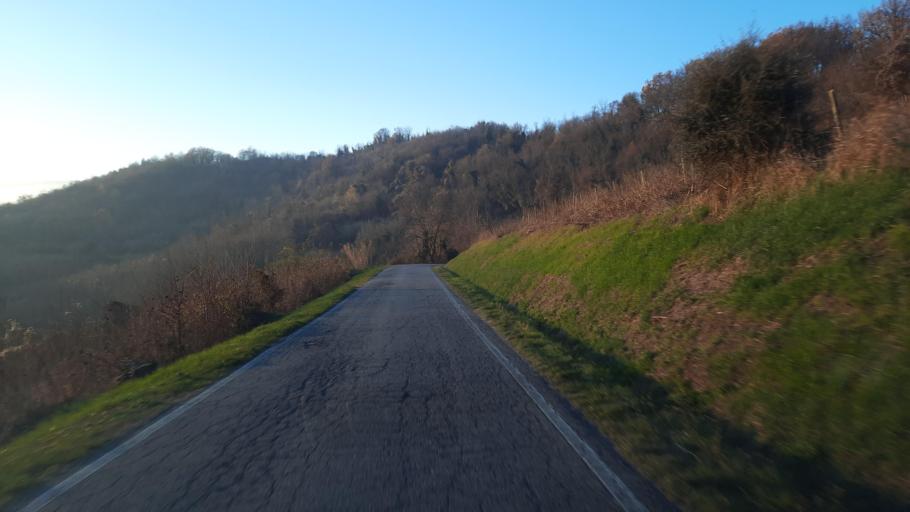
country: IT
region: Piedmont
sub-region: Provincia di Alessandria
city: Camino
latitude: 45.1619
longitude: 8.2799
